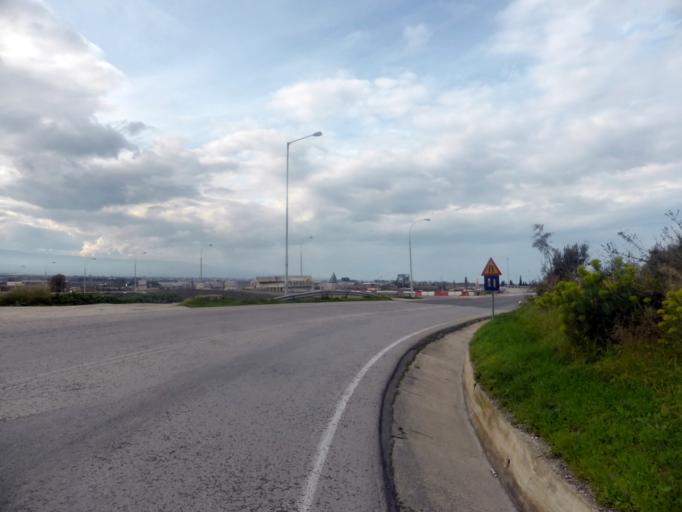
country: GR
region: Peloponnese
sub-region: Nomos Korinthias
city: Arkhaia Korinthos
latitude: 37.9134
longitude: 22.8858
